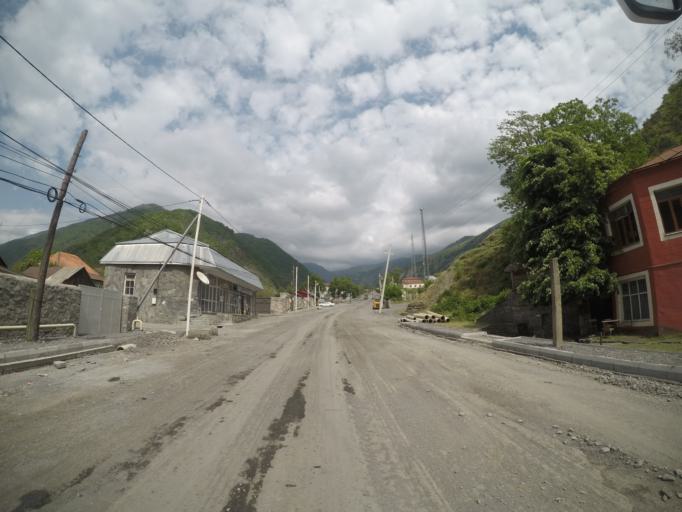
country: AZ
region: Qakh Rayon
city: Qaxbas
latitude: 41.4681
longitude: 47.0549
